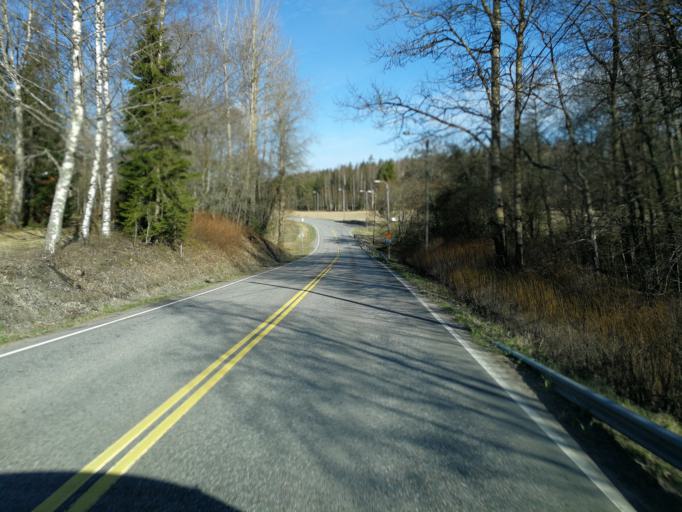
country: FI
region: Uusimaa
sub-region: Helsinki
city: Kirkkonummi
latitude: 60.2042
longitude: 24.5018
